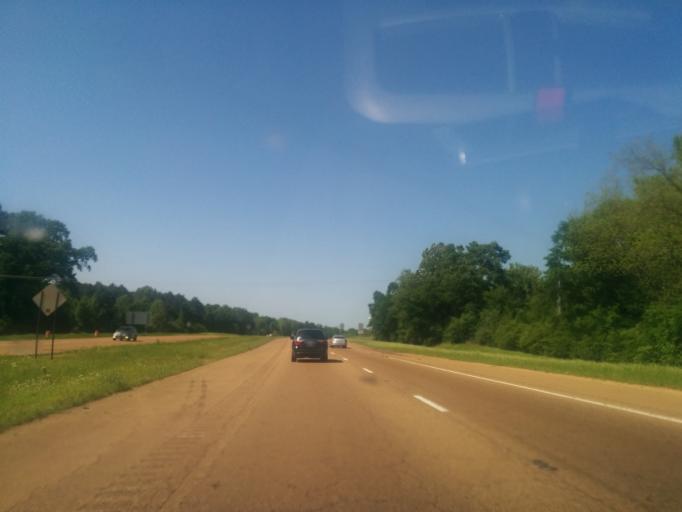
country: US
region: Mississippi
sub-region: Madison County
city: Madison
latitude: 32.4789
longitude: -90.1302
